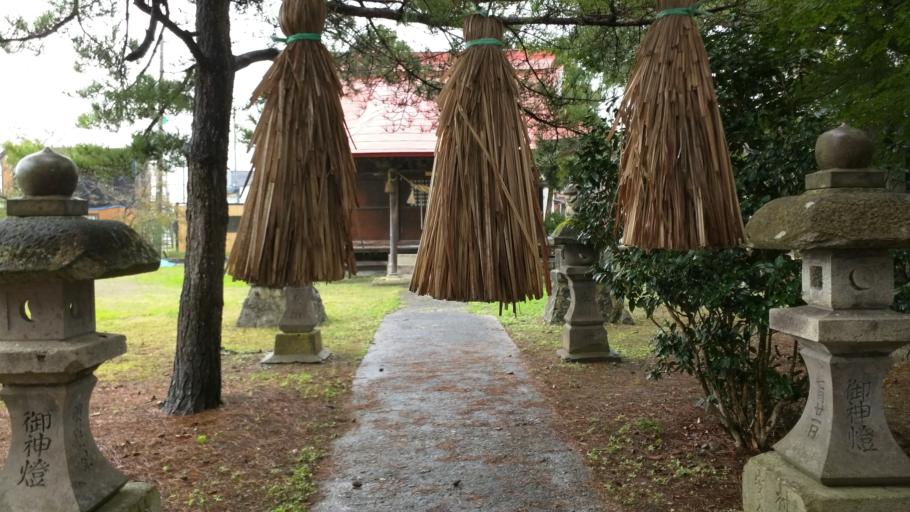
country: JP
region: Fukushima
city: Kitakata
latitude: 37.5218
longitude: 139.8938
